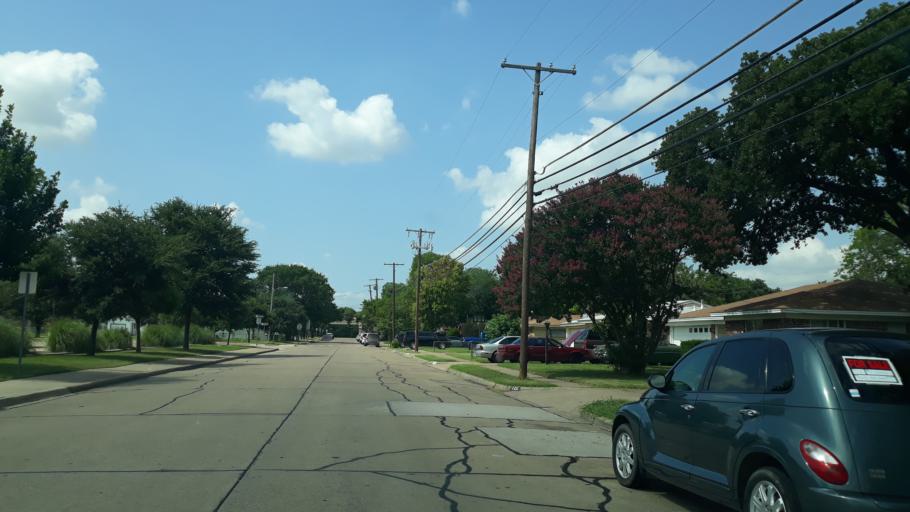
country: US
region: Texas
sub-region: Dallas County
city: Irving
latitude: 32.8128
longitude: -96.9817
